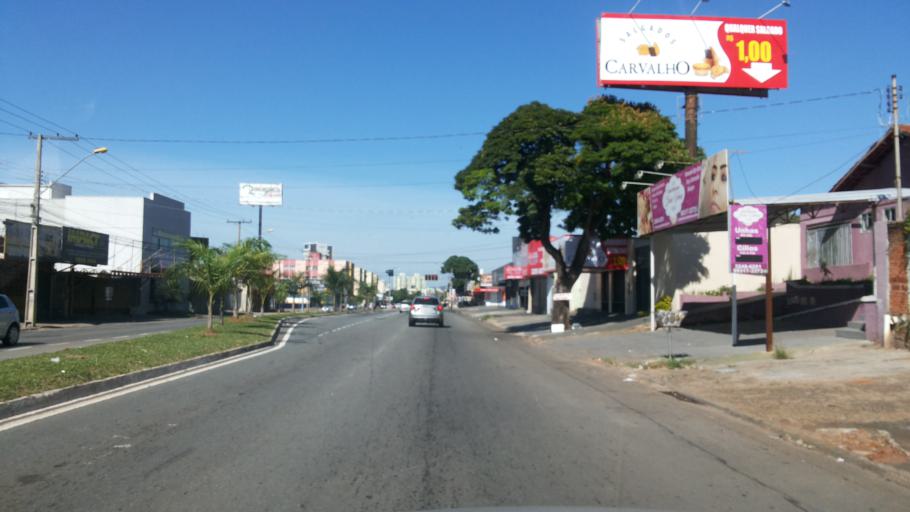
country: BR
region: Goias
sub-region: Goiania
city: Goiania
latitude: -16.7244
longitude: -49.2612
